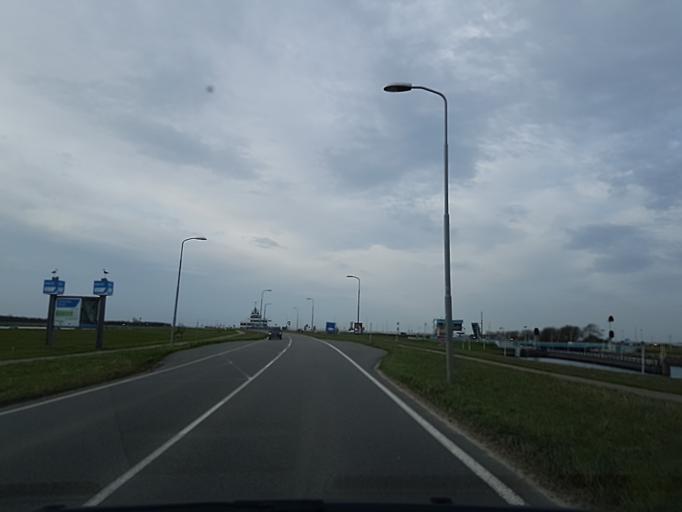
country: NL
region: Zeeland
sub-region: Gemeente Terneuzen
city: Terneuzen
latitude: 51.3319
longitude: 3.8172
